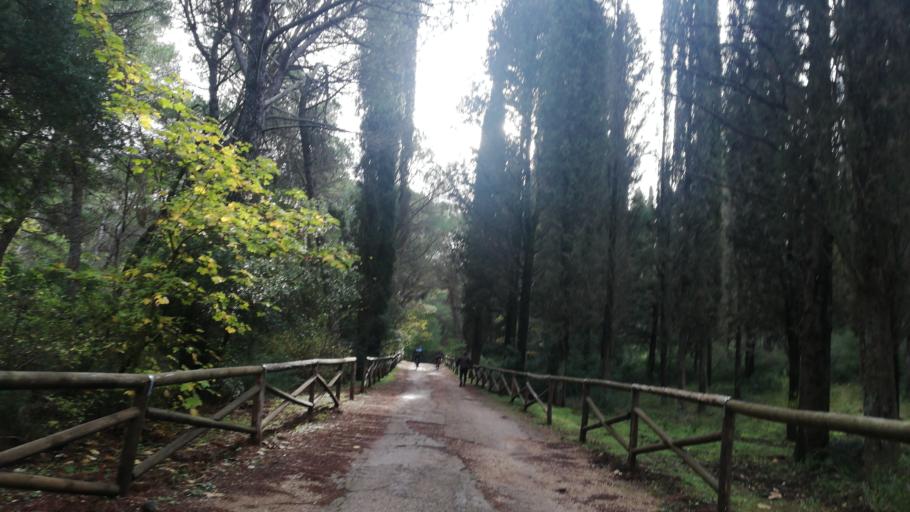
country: IT
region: Apulia
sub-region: Provincia di Bari
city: Cassano delle Murge
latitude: 40.8870
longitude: 16.7013
